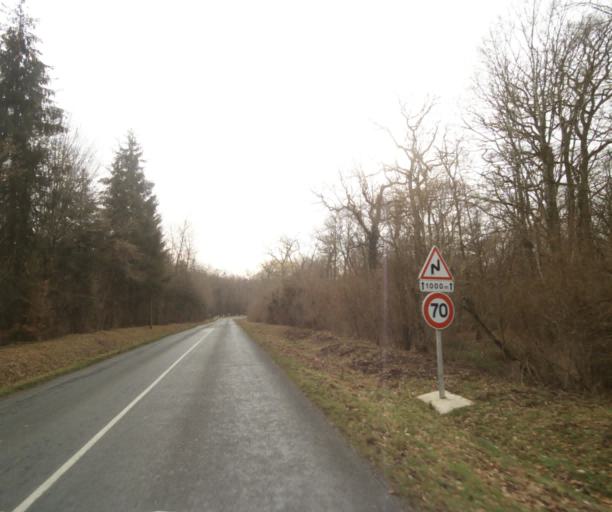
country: FR
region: Champagne-Ardenne
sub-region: Departement de la Haute-Marne
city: Villiers-en-Lieu
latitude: 48.6995
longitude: 4.8958
